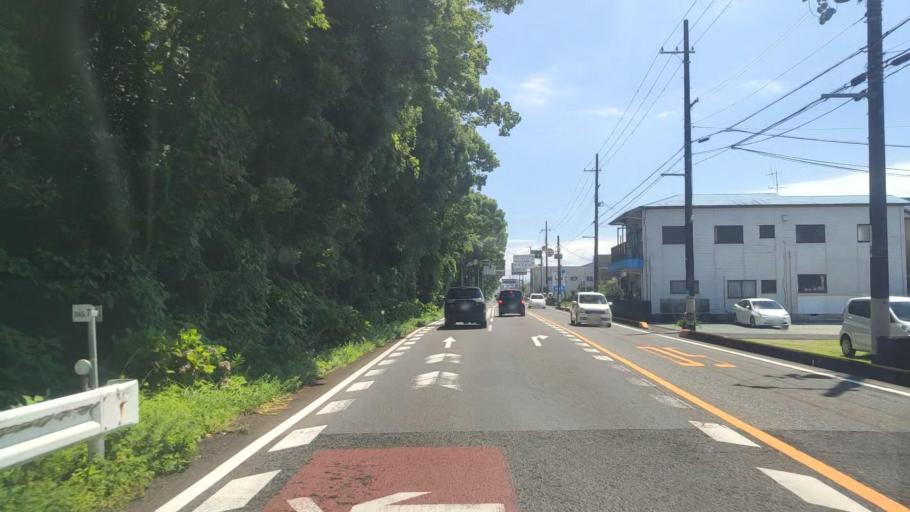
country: JP
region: Wakayama
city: Shingu
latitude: 33.8704
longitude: 136.0842
